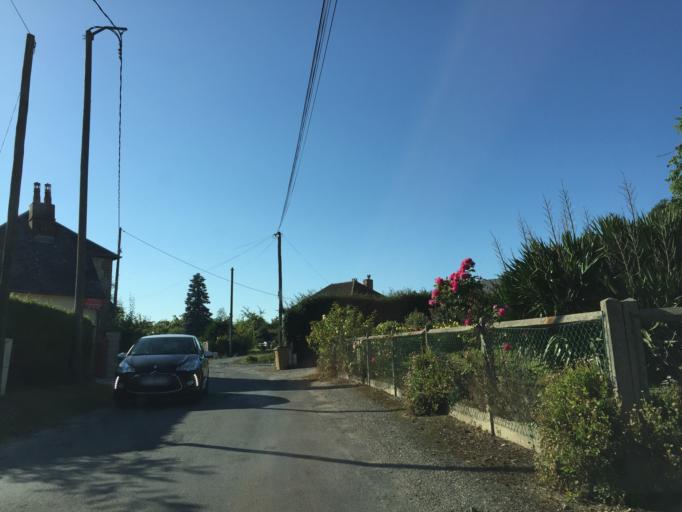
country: FR
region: Lower Normandy
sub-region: Departement du Calvados
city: Equemauville
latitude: 49.3940
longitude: 0.2034
